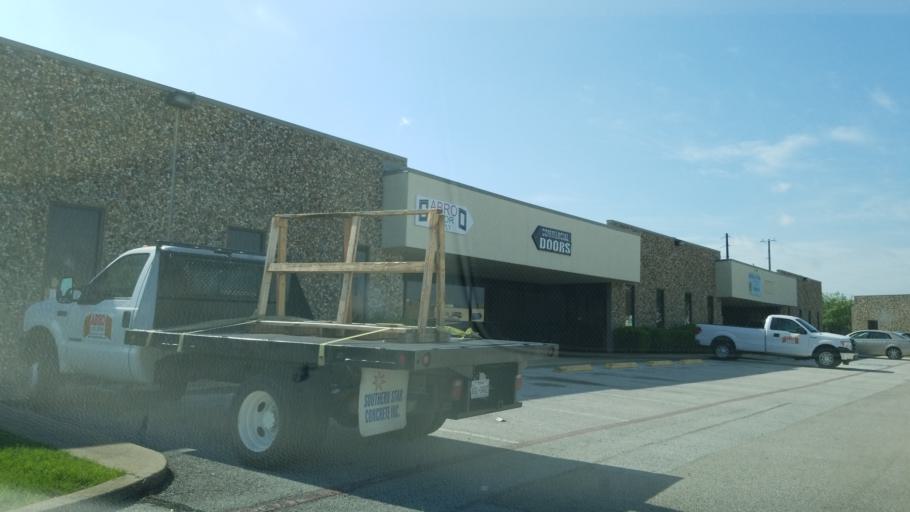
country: US
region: Texas
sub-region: Dallas County
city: Farmers Branch
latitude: 32.8804
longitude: -96.8887
